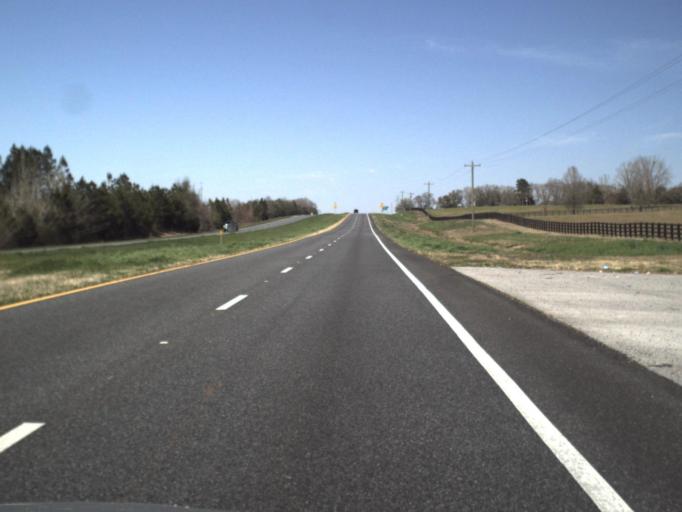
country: US
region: Florida
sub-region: Jackson County
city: Graceville
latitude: 30.8810
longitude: -85.3646
